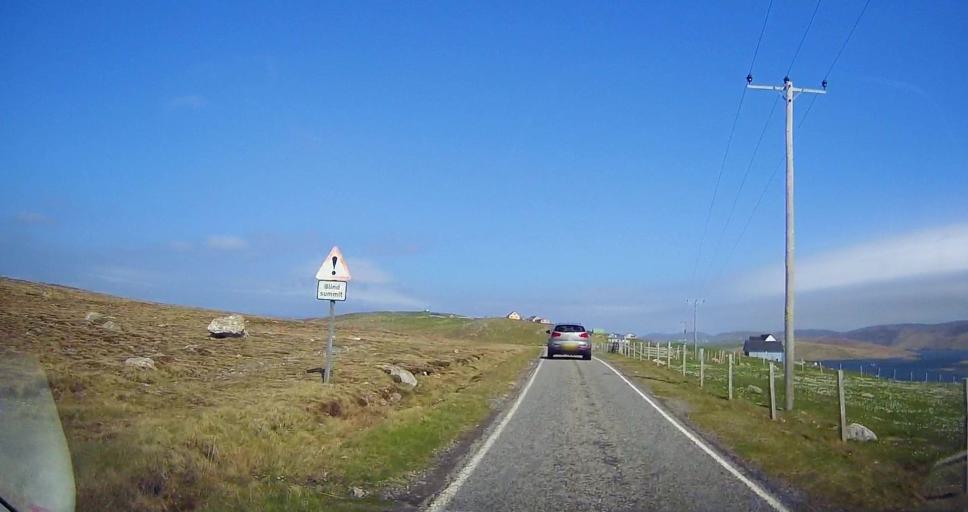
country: GB
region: Scotland
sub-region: Shetland Islands
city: Sandwick
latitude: 60.0911
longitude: -1.3251
